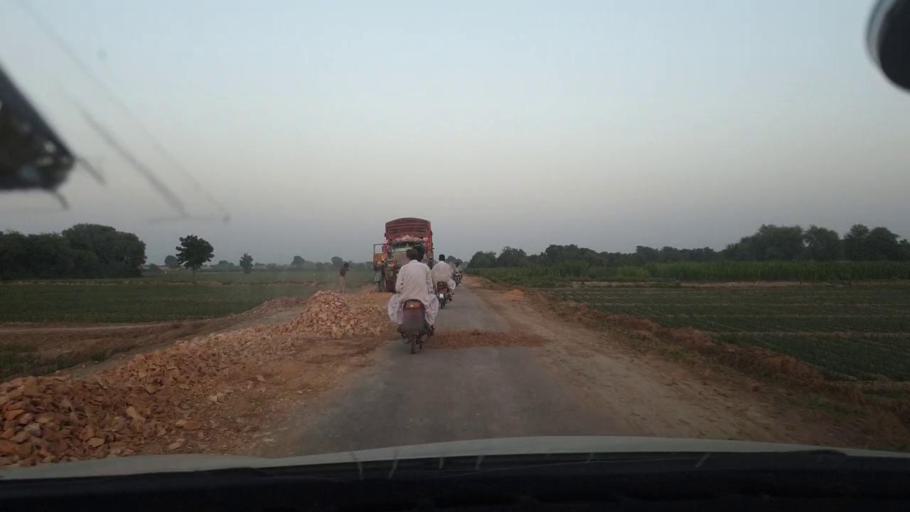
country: PK
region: Sindh
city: Bhit Shah
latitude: 25.7528
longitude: 68.5395
